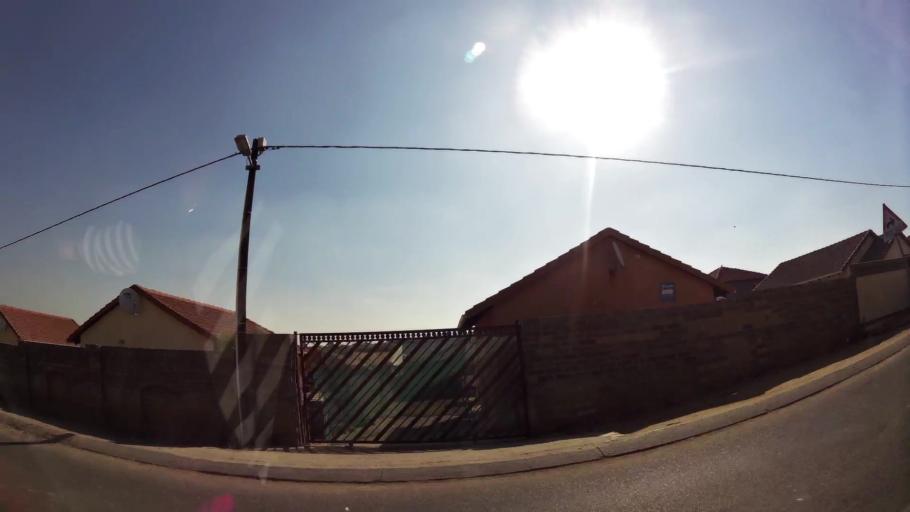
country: ZA
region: Gauteng
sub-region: West Rand District Municipality
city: Muldersdriseloop
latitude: -26.0390
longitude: 27.9210
